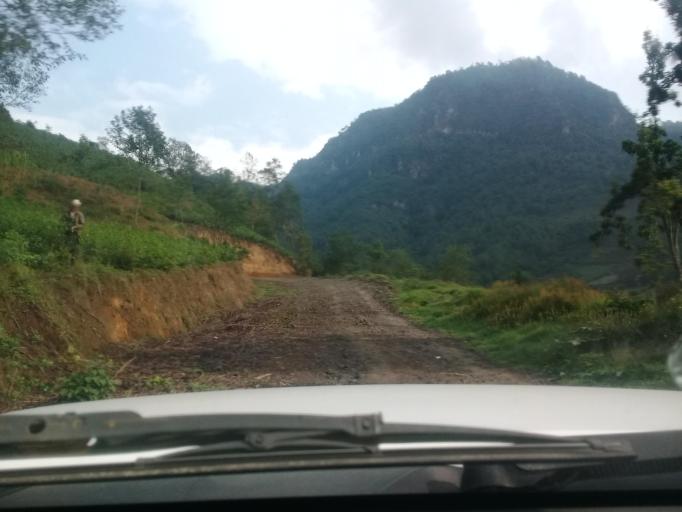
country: MX
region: Veracruz
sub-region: Mariano Escobedo
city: San Isidro el Berro
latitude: 18.9547
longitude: -97.2008
